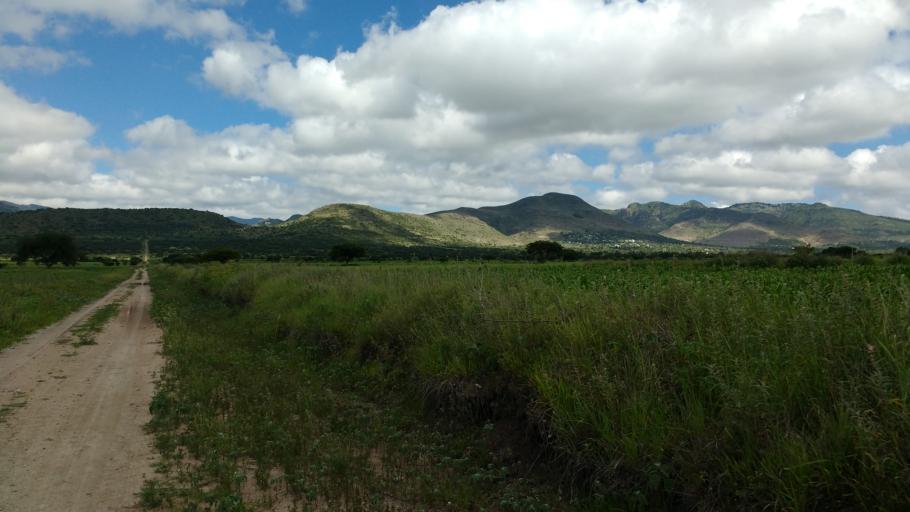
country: MX
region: Hidalgo
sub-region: Tezontepec de Aldama
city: Tenango
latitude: 20.2468
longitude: -99.2571
